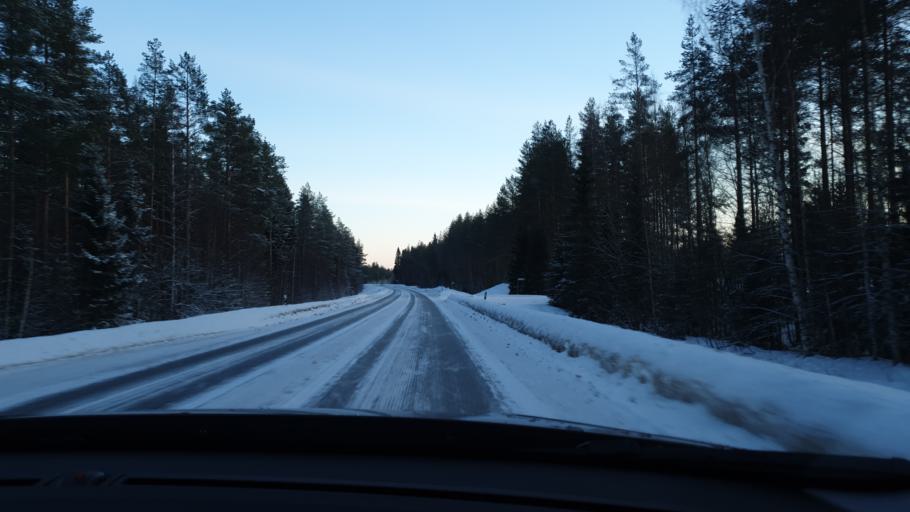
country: FI
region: Kainuu
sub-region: Kajaani
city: Sotkamo
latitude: 64.0818
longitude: 28.6083
